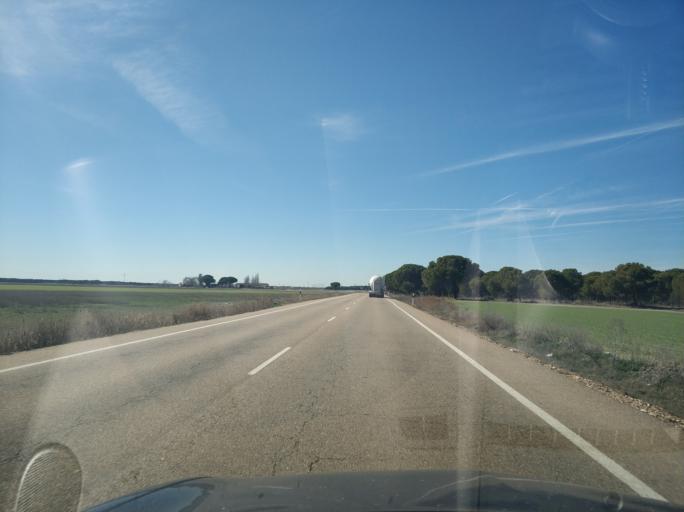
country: ES
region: Castille and Leon
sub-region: Provincia de Valladolid
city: Aldeamayor de San Martin
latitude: 41.5562
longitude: -4.6344
